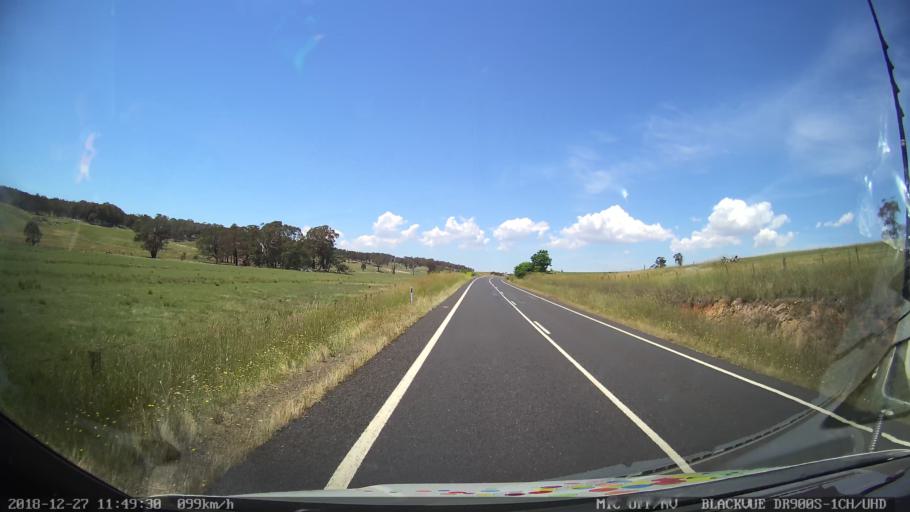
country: AU
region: New South Wales
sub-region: Bathurst Regional
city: Perthville
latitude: -33.6207
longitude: 149.4355
